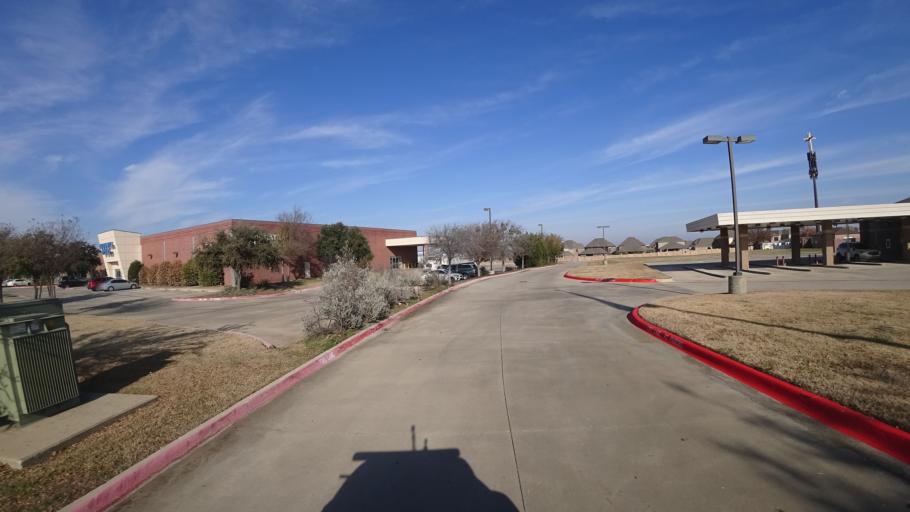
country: US
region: Texas
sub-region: Denton County
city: Lewisville
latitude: 33.0439
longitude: -97.0171
